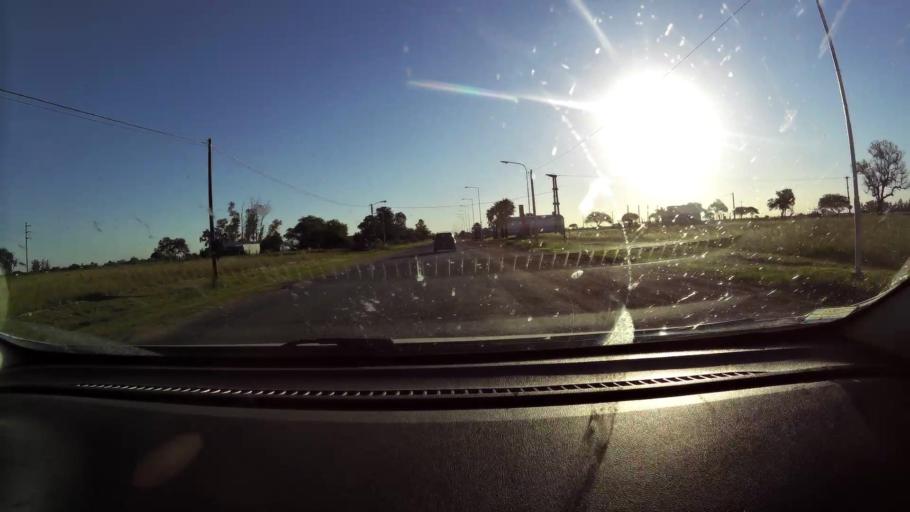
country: AR
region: Cordoba
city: Las Varas
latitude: -31.8034
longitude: -62.6220
